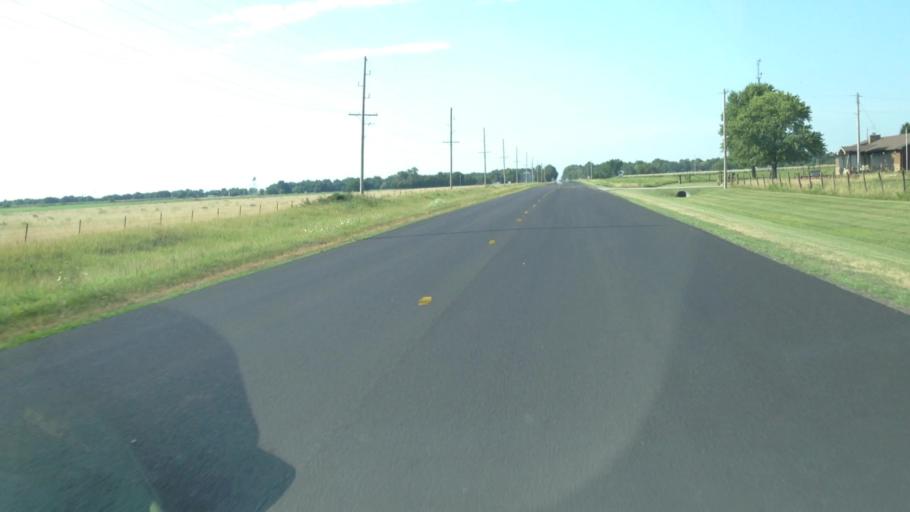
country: US
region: Kansas
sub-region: Allen County
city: Iola
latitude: 37.9001
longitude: -95.1704
